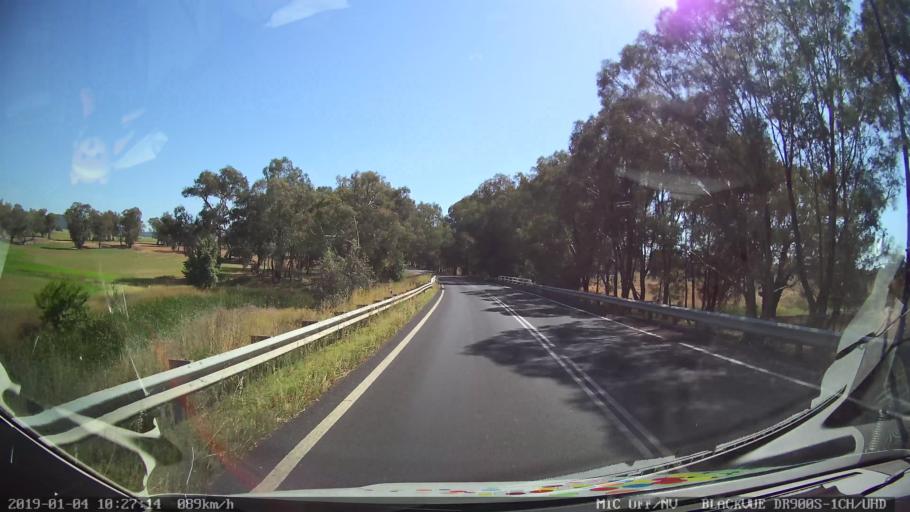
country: AU
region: New South Wales
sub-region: Cabonne
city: Canowindra
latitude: -33.3726
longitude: 148.5968
